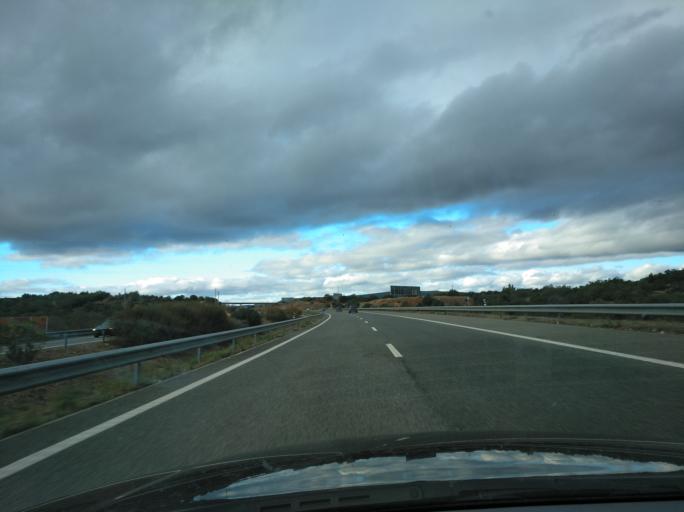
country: PT
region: Faro
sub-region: Albufeira
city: Ferreiras
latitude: 37.1818
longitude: -8.2162
